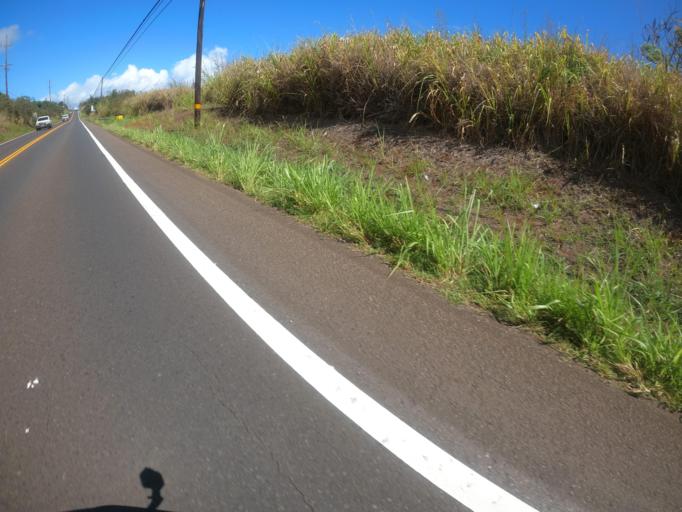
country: US
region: Hawaii
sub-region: Honolulu County
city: Schofield Barracks
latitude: 21.4538
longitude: -158.0596
